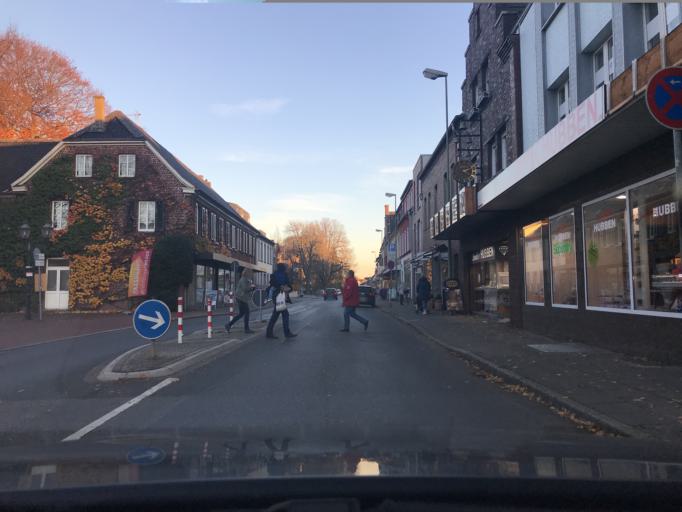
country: DE
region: North Rhine-Westphalia
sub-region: Regierungsbezirk Dusseldorf
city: Kamp-Lintfort
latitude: 51.4385
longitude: 6.5323
